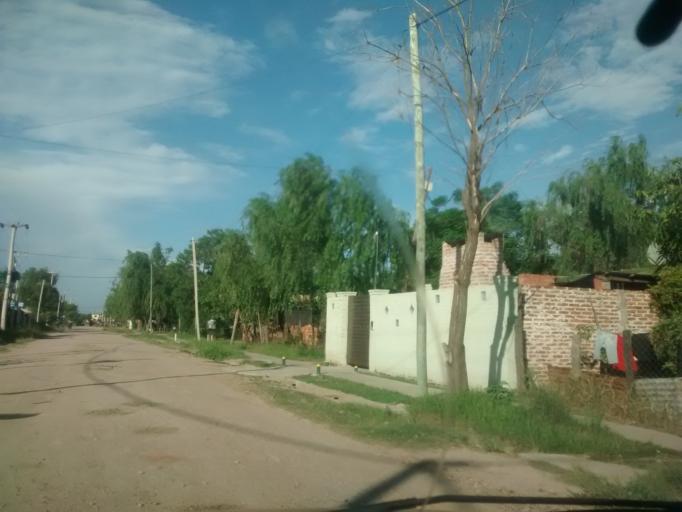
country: AR
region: Chaco
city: Fontana
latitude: -27.4568
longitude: -59.0298
